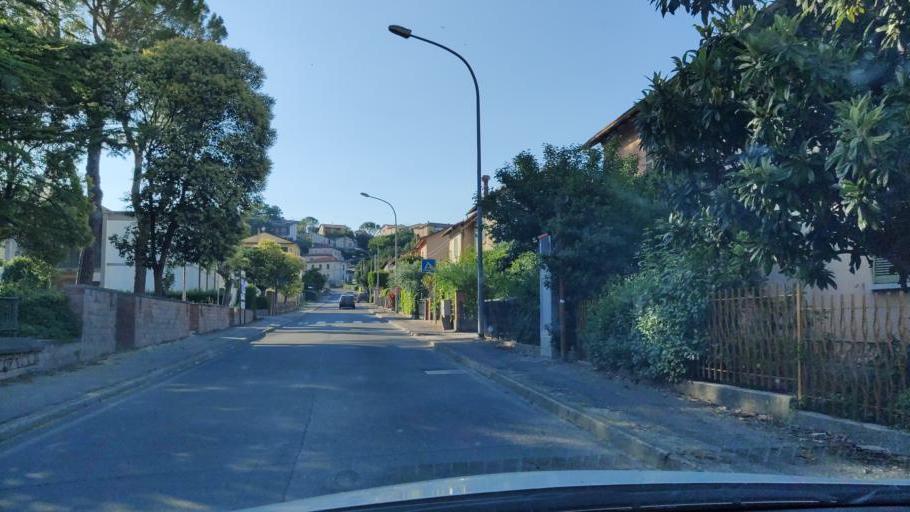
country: IT
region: Umbria
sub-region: Provincia di Terni
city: Narni Scalo
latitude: 42.5382
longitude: 12.5197
